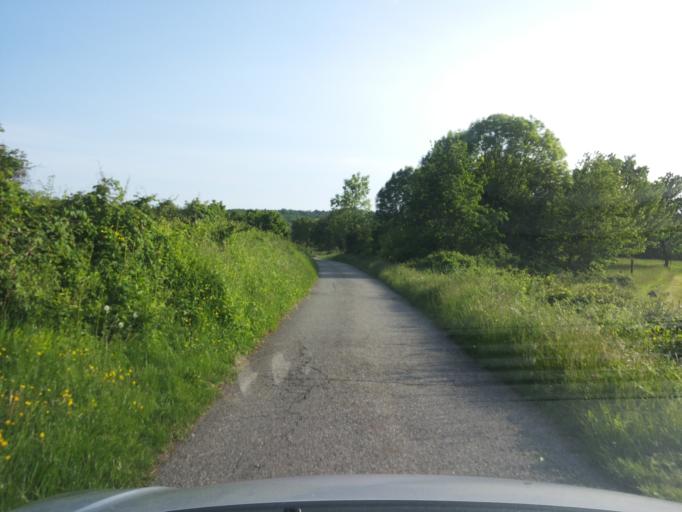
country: IT
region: Piedmont
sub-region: Provincia di Torino
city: Cossano Canavese
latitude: 45.3919
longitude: 8.0040
